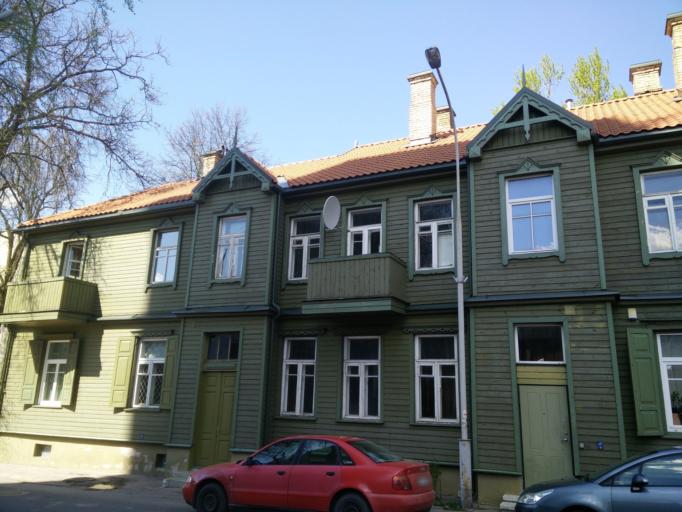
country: LT
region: Vilnius County
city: Vilkpede
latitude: 54.6823
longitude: 25.2513
